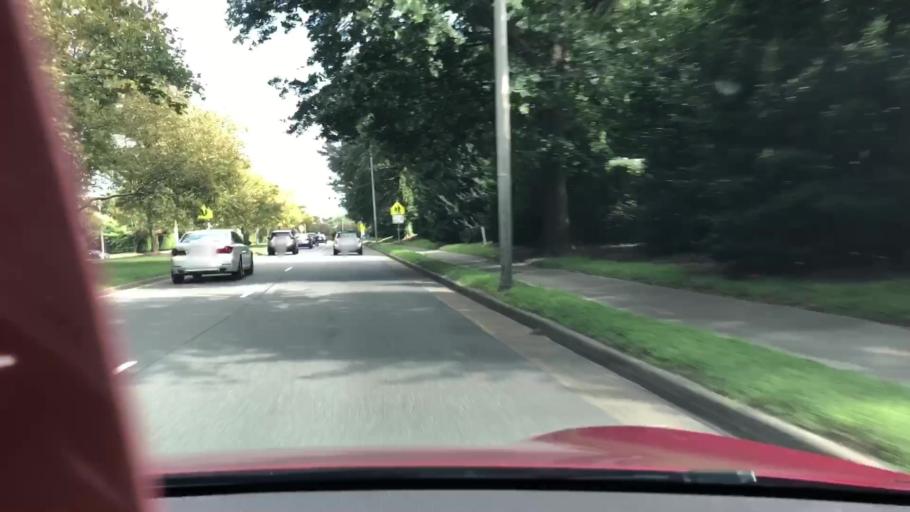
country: US
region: Virginia
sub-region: City of Virginia Beach
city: Virginia Beach
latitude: 36.8906
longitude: -76.0535
